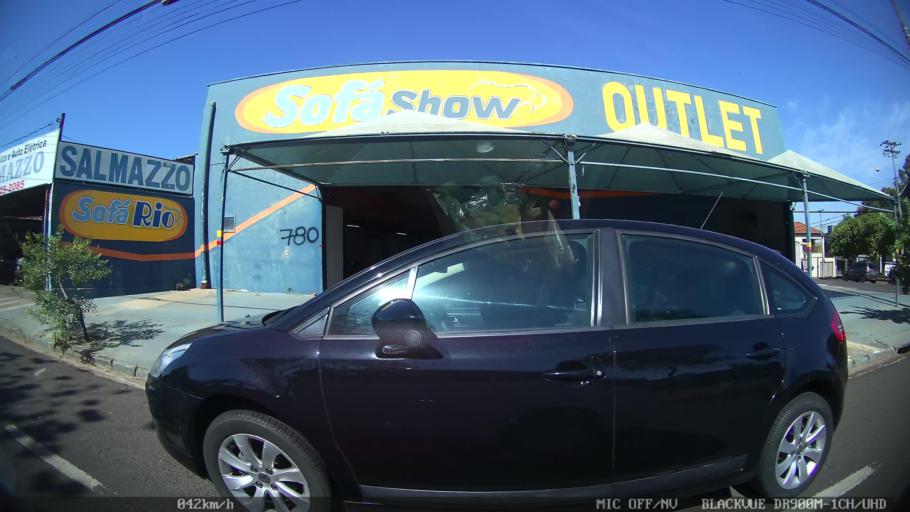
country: BR
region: Sao Paulo
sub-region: Sao Jose Do Rio Preto
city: Sao Jose do Rio Preto
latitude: -20.7800
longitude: -49.3748
